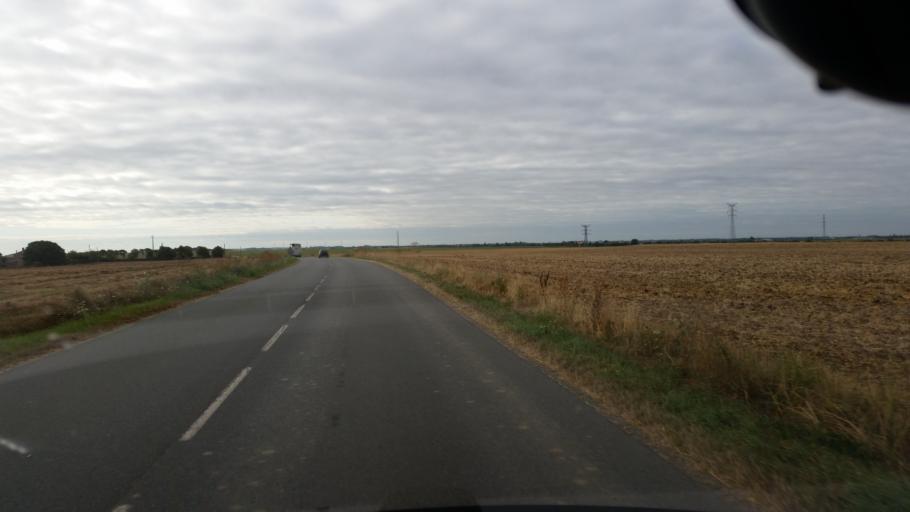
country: FR
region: Poitou-Charentes
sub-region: Departement de la Charente-Maritime
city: Marans
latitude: 46.3004
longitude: -0.9809
